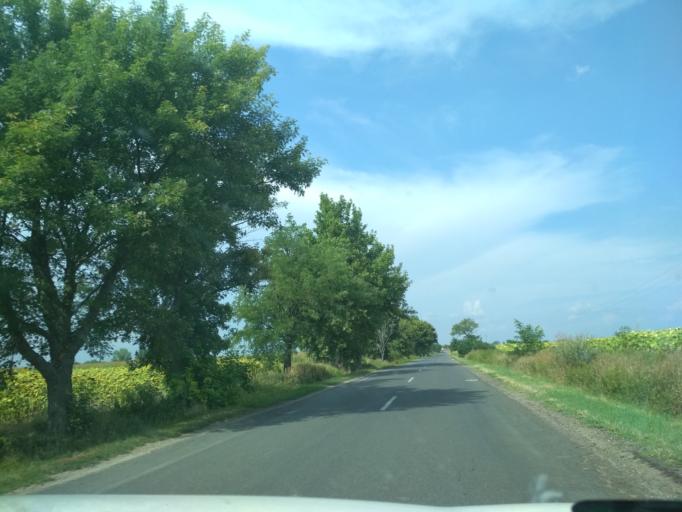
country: HU
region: Jasz-Nagykun-Szolnok
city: Tiszaszolos
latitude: 47.5413
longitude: 20.7183
